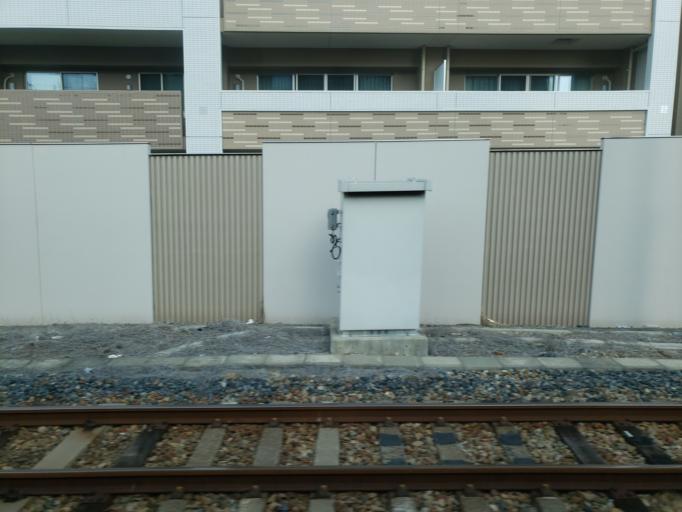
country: JP
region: Hyogo
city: Kobe
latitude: 34.7076
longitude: 135.2215
